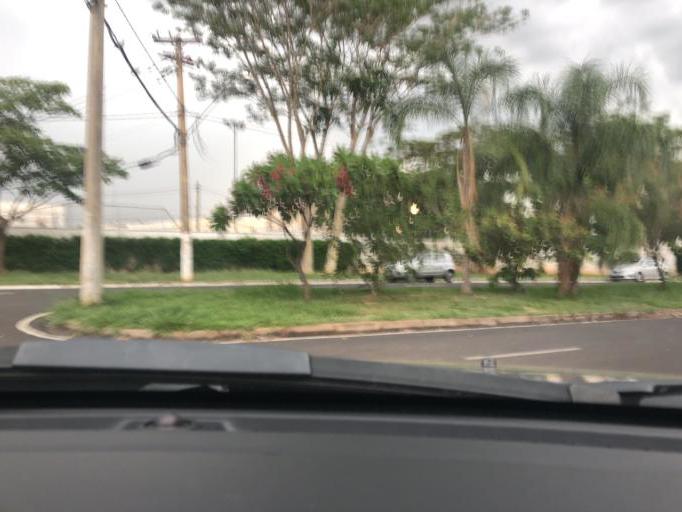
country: BR
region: Sao Paulo
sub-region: Sao Jose Do Rio Preto
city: Sao Jose do Rio Preto
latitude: -20.8409
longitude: -49.3858
